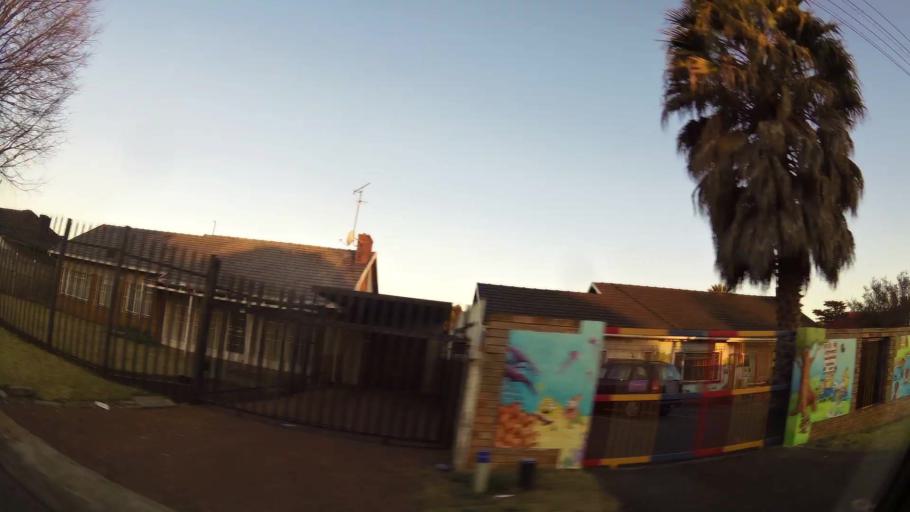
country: ZA
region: Gauteng
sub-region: Ekurhuleni Metropolitan Municipality
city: Germiston
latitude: -26.2702
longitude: 28.1544
